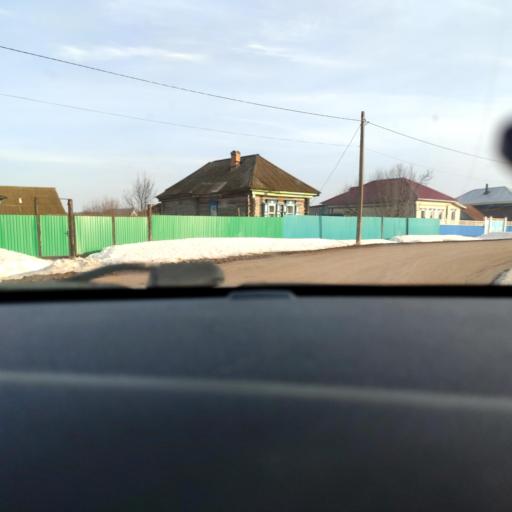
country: RU
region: Bashkortostan
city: Avdon
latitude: 54.4841
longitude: 55.5953
